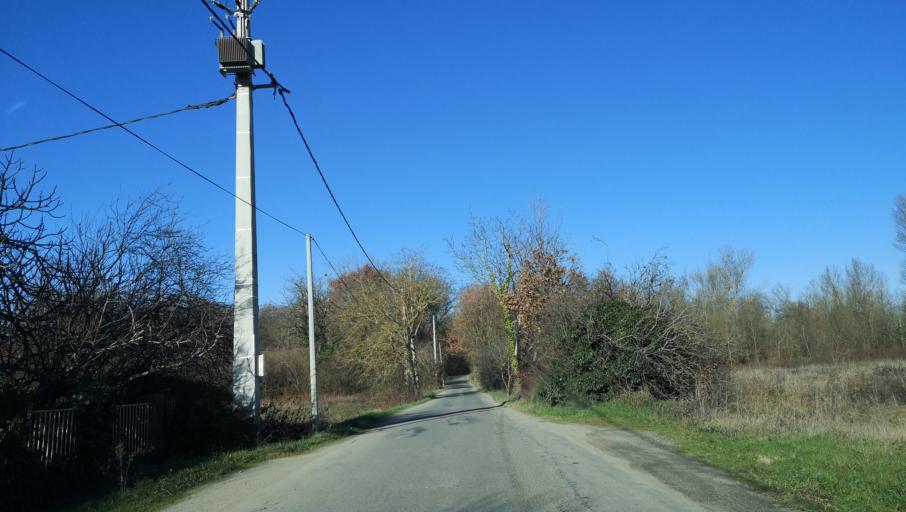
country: FR
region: Midi-Pyrenees
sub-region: Departement de la Haute-Garonne
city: Beauzelle
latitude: 43.6598
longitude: 1.3940
